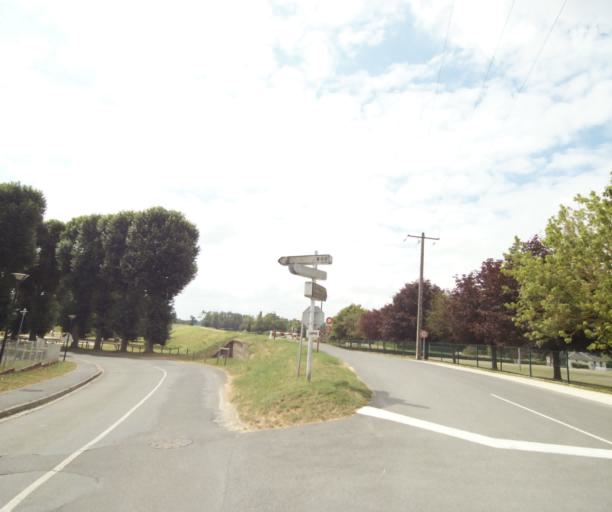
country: FR
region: Centre
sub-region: Departement du Loiret
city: Checy
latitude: 47.8902
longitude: 2.0273
